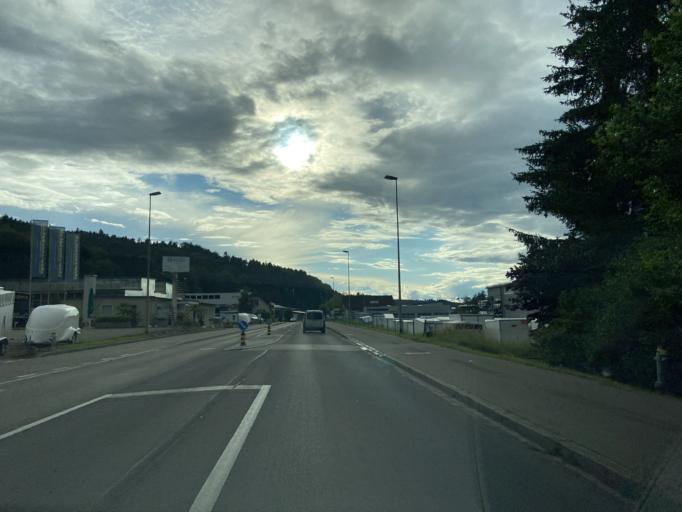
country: CH
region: Zurich
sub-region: Bezirk Winterthur
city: Elsau-Raeterschen / Raeterschen
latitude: 47.4991
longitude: 8.7917
